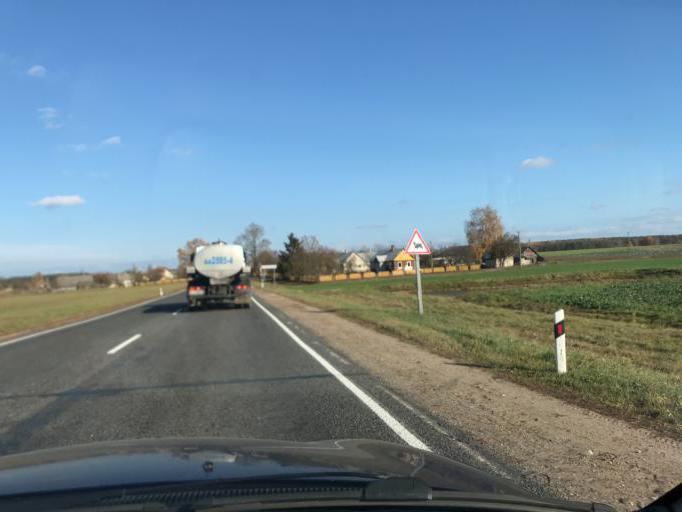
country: BY
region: Grodnenskaya
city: Lida
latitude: 54.0110
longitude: 25.2174
